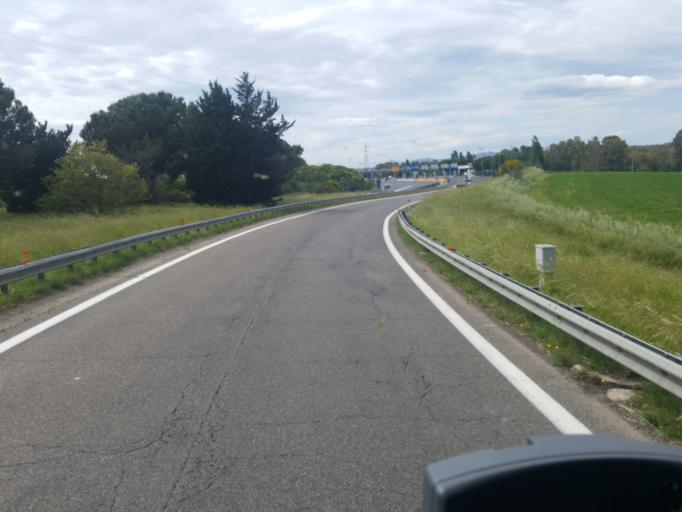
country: IT
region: Latium
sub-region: Citta metropolitana di Roma Capitale
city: Ara Nova
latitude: 41.9135
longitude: 12.2146
